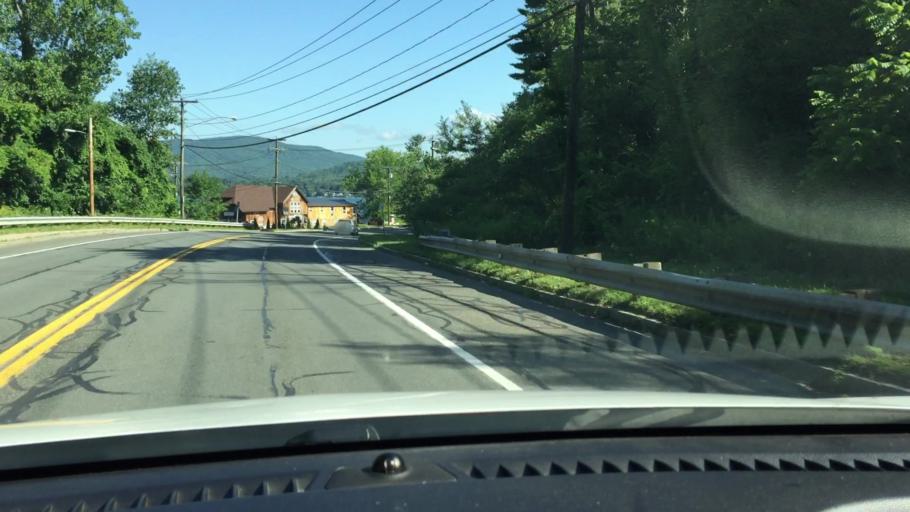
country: US
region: Massachusetts
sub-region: Berkshire County
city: Lanesborough
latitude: 42.4872
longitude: -73.2464
